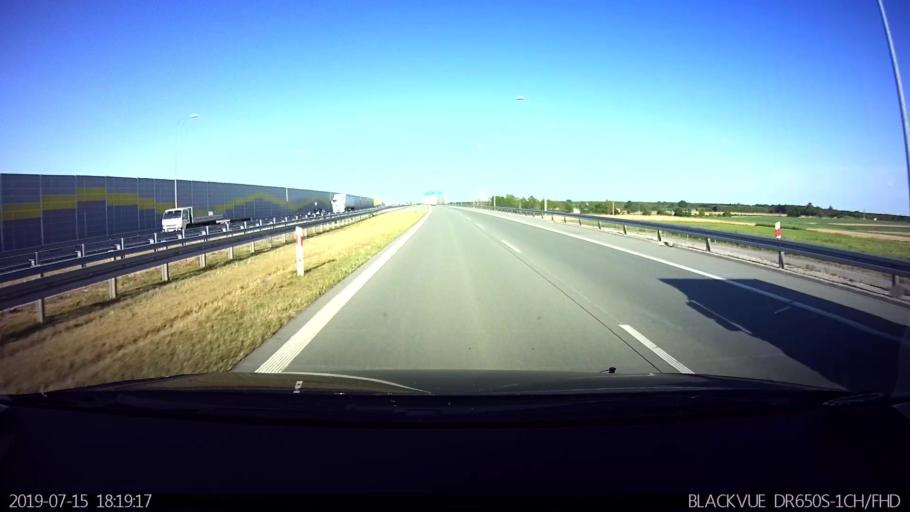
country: PL
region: Lodz Voivodeship
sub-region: Powiat laski
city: Sedziejowice
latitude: 51.5591
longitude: 19.0156
